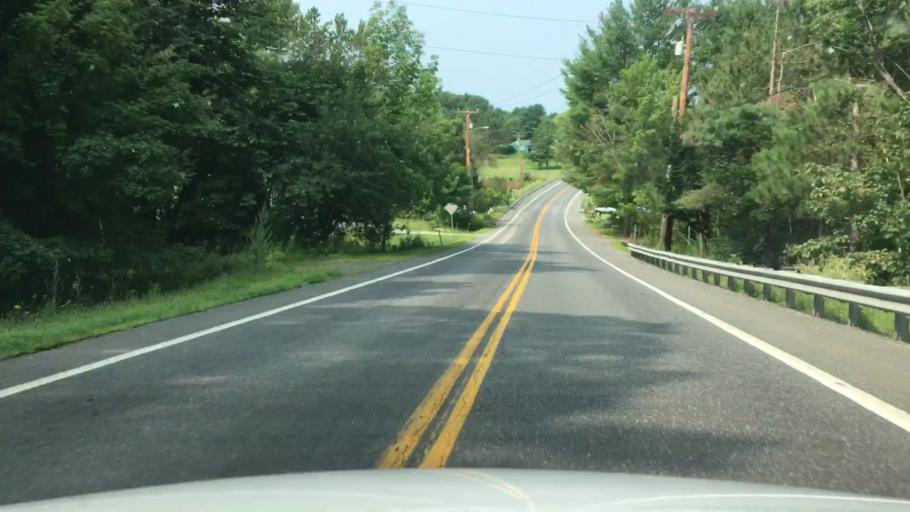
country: US
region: Maine
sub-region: Kennebec County
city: Augusta
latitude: 44.3171
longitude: -69.7256
